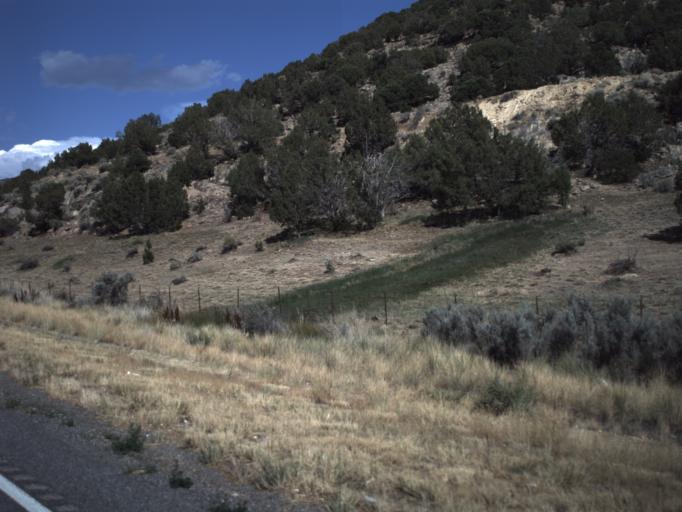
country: US
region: Utah
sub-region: Sanpete County
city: Manti
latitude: 39.2408
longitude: -111.6552
